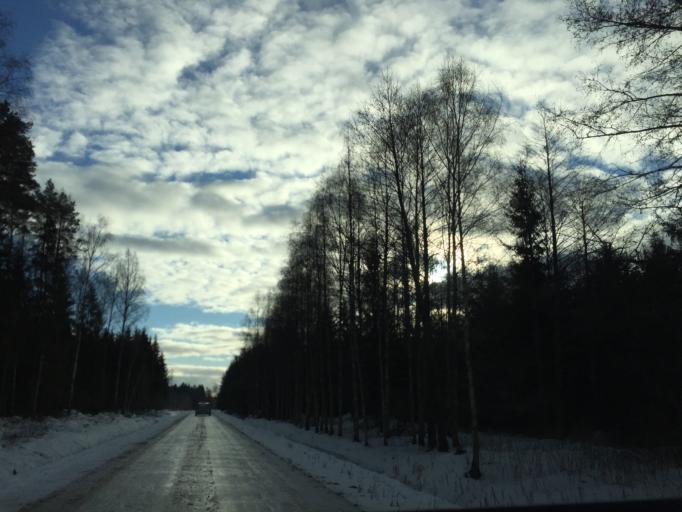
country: LV
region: Ogre
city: Jumprava
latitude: 56.5521
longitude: 24.8578
